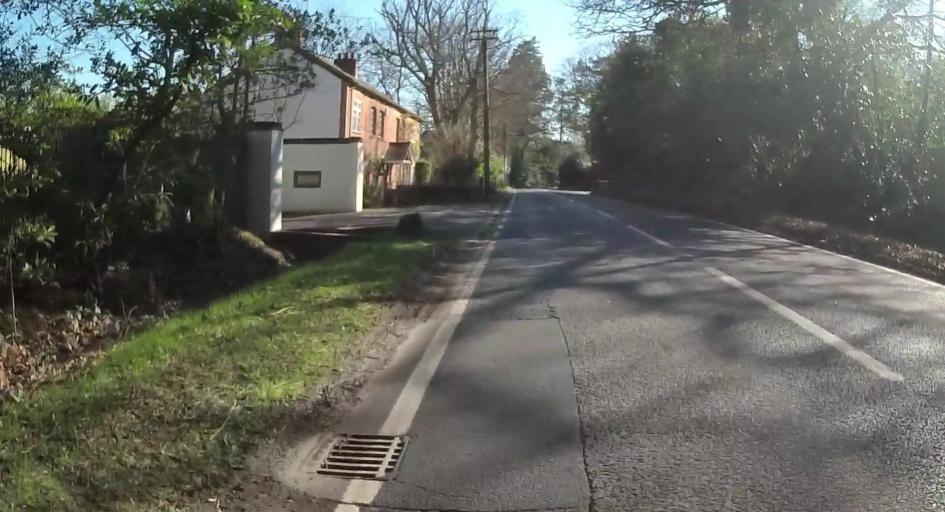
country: GB
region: England
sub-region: Royal Borough of Windsor and Maidenhead
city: Ascot
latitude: 51.3853
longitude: -0.6709
